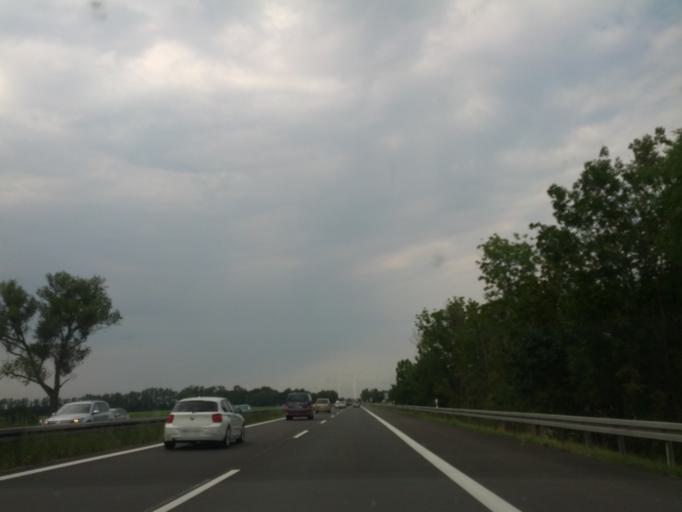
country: DE
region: Brandenburg
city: Dabergotz
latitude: 52.8811
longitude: 12.7568
